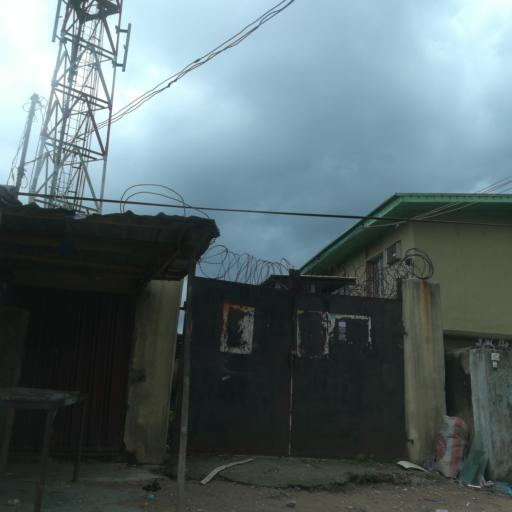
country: NG
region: Lagos
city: Agege
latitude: 6.6063
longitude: 3.3088
